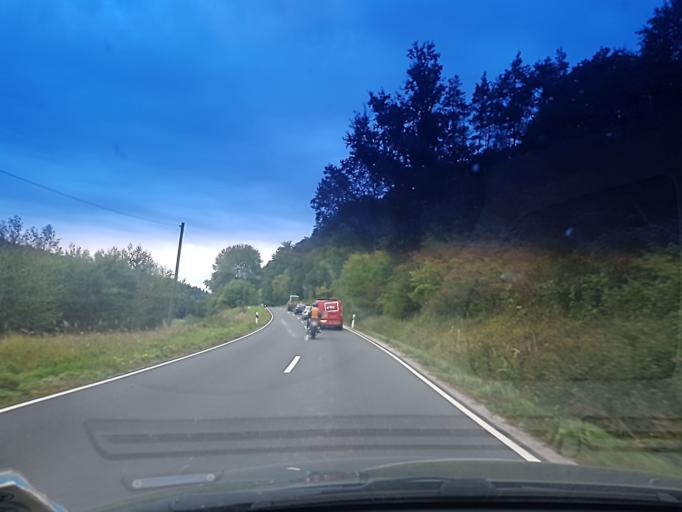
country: DE
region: Bavaria
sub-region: Upper Franconia
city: Burgwindheim
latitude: 49.8357
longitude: 10.5423
